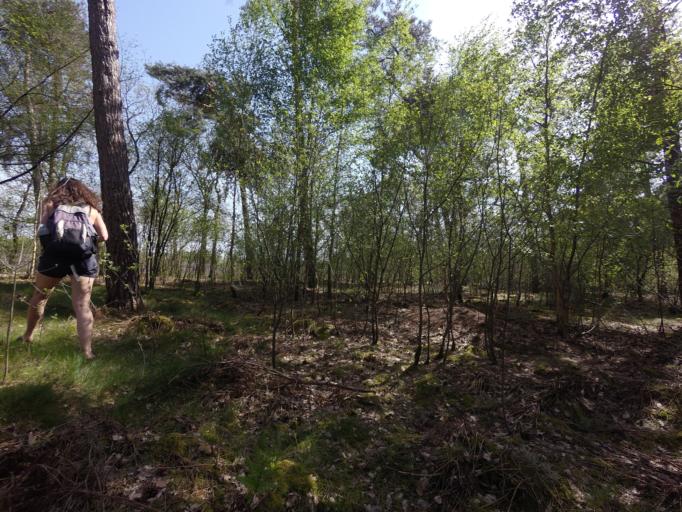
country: NL
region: North Brabant
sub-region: Gemeente Goirle
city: Goirle
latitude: 51.4781
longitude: 5.0116
